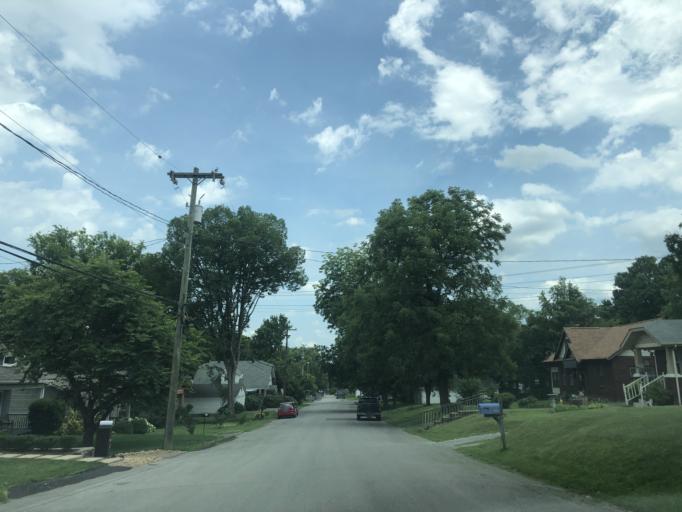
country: US
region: Tennessee
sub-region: Davidson County
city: Nashville
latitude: 36.1858
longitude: -86.7423
